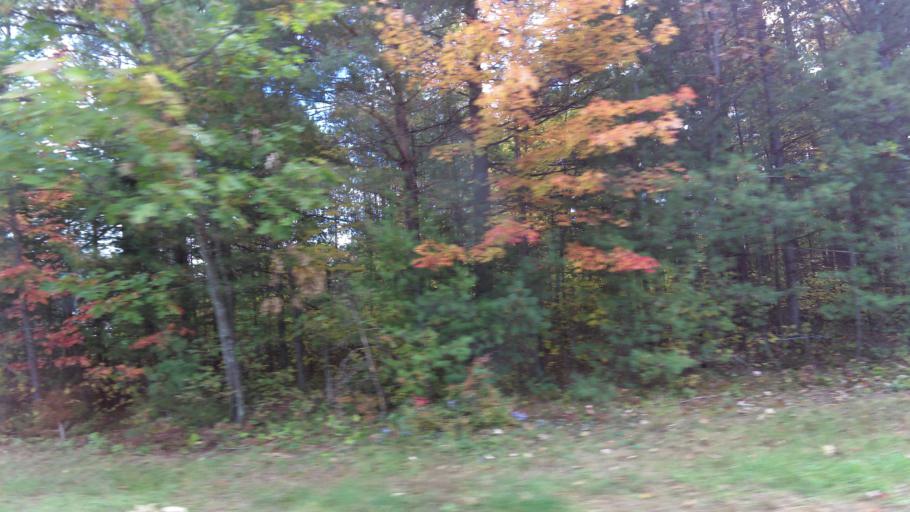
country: CA
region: Ontario
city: Deep River
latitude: 46.0972
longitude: -77.4883
